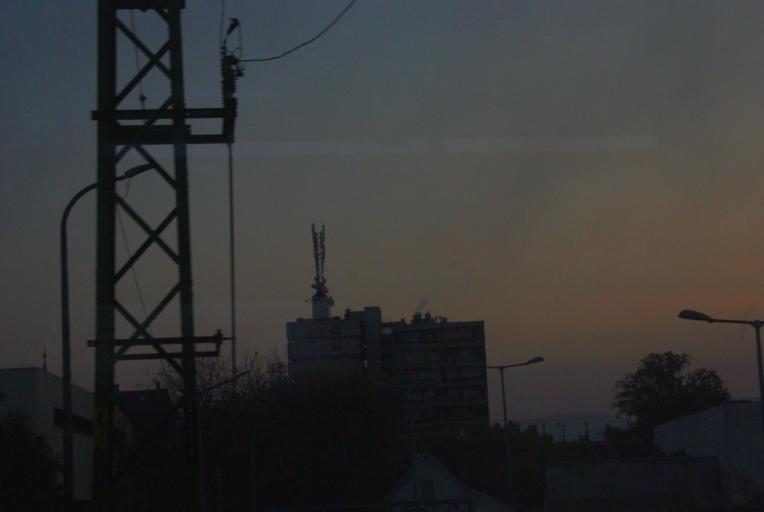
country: HU
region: Pest
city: Vac
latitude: 47.7830
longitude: 19.1314
